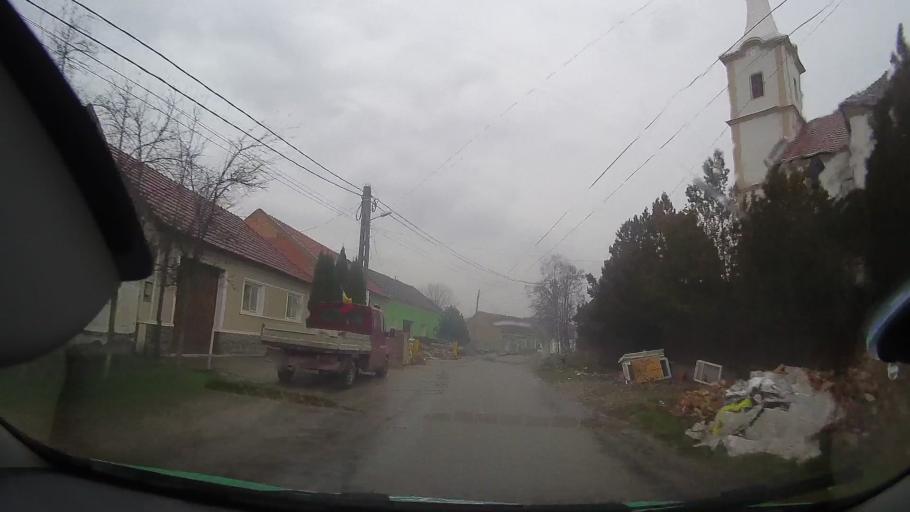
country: RO
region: Bihor
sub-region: Comuna Uileacu de Beius
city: Uileacu de Beius
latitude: 46.6853
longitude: 22.2200
